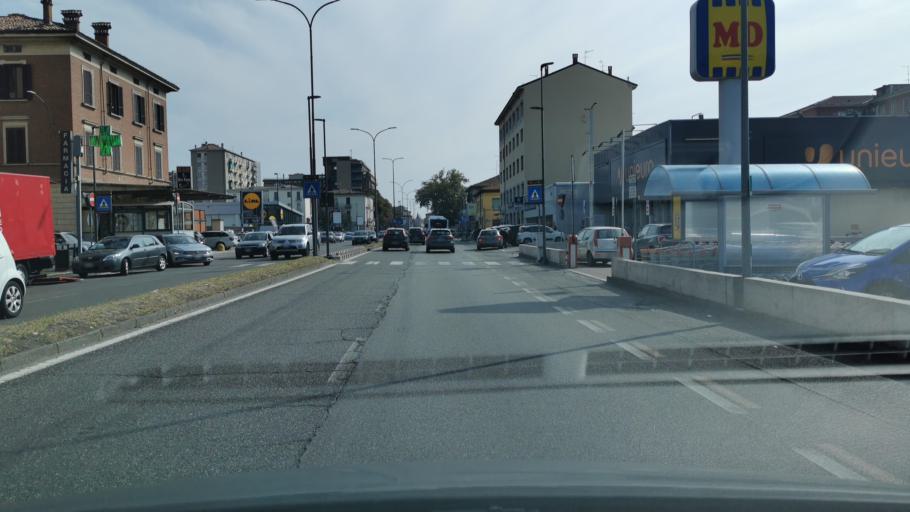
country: IT
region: Emilia-Romagna
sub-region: Provincia di Piacenza
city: Piacenza
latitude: 45.0543
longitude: 9.6732
